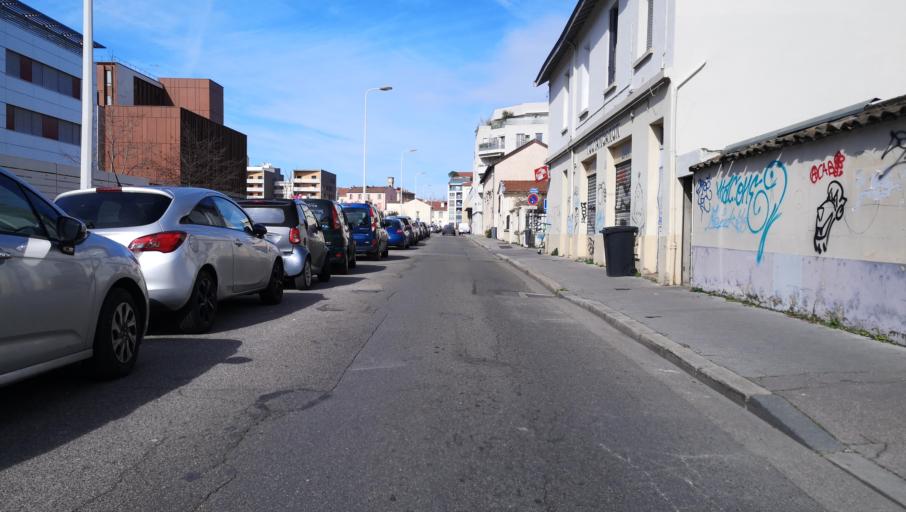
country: FR
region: Rhone-Alpes
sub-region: Departement du Rhone
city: Villeurbanne
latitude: 45.7467
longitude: 4.8774
